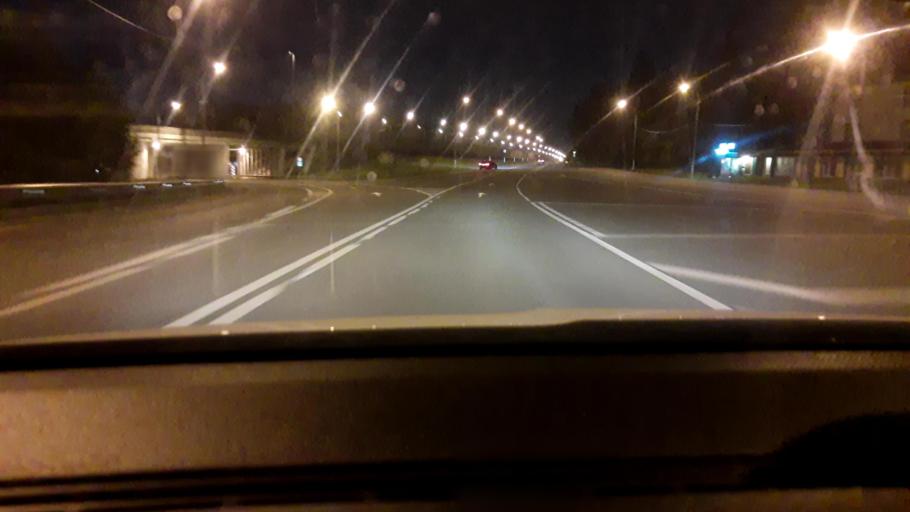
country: RU
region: Moskovskaya
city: Pavlovskaya Sloboda
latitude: 55.7838
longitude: 37.0827
